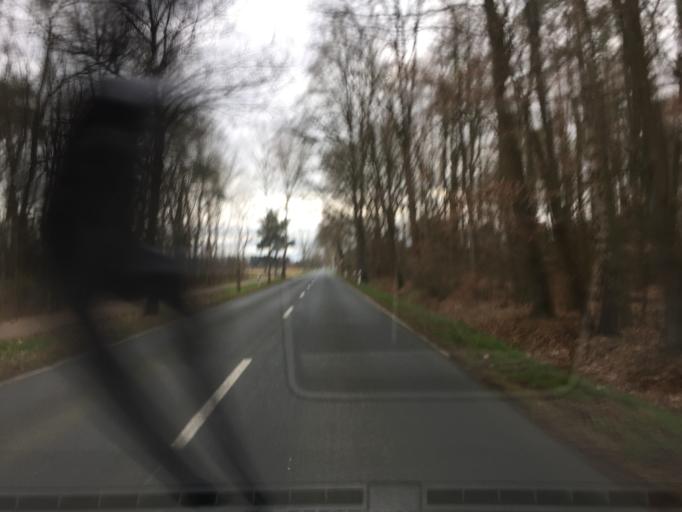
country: DE
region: Lower Saxony
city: Neustadt am Rubenberge
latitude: 52.4815
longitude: 9.4946
